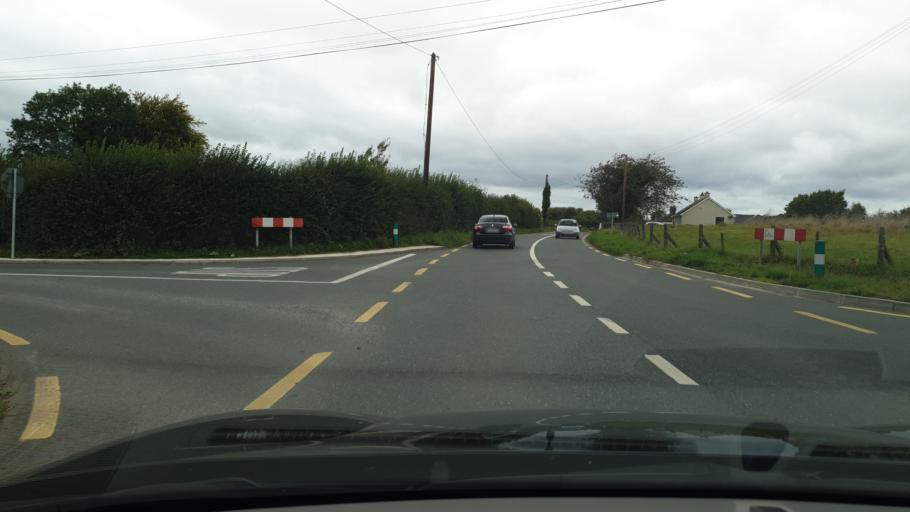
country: IE
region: Leinster
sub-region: Kildare
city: Clane
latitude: 53.2775
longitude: -6.6960
